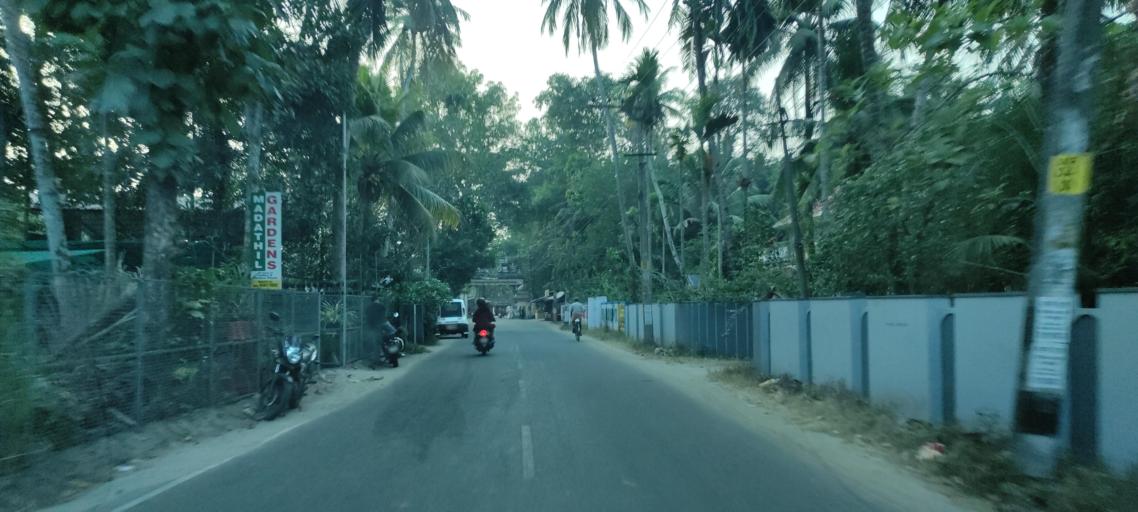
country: IN
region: Kerala
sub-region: Alappuzha
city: Kayankulam
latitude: 9.1252
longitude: 76.4969
